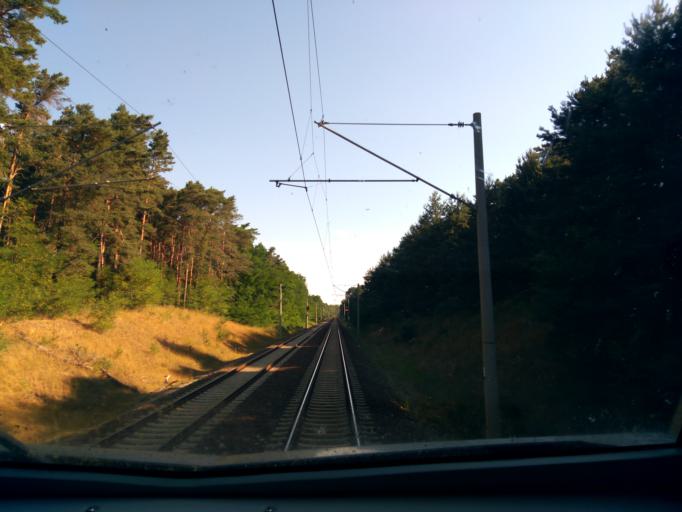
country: DE
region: Brandenburg
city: Halbe
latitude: 52.0459
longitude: 13.7199
